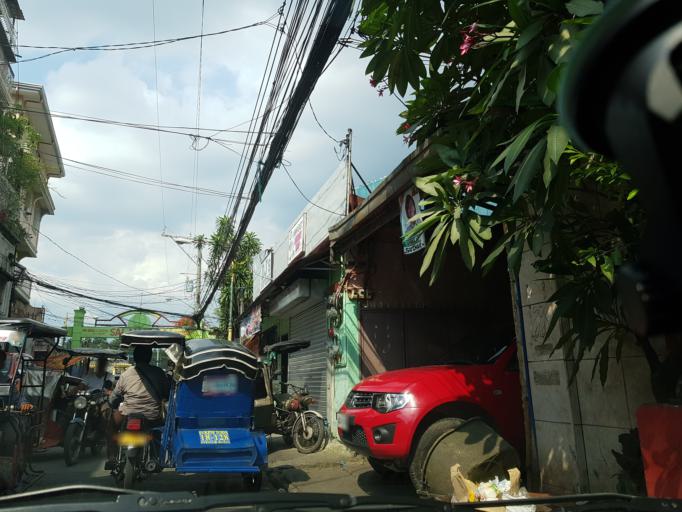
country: PH
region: Calabarzon
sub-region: Province of Rizal
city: Pateros
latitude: 14.5620
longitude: 121.0894
